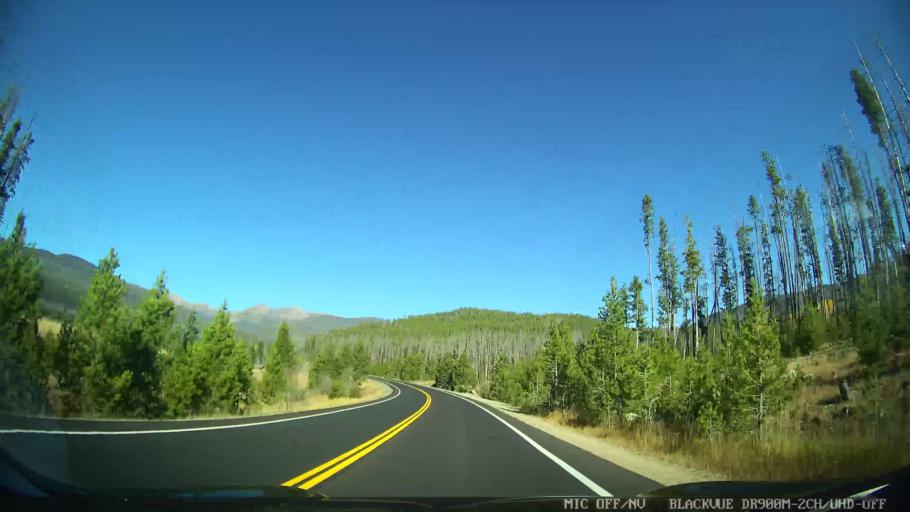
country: US
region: Colorado
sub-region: Grand County
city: Granby
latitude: 40.3173
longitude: -105.8448
